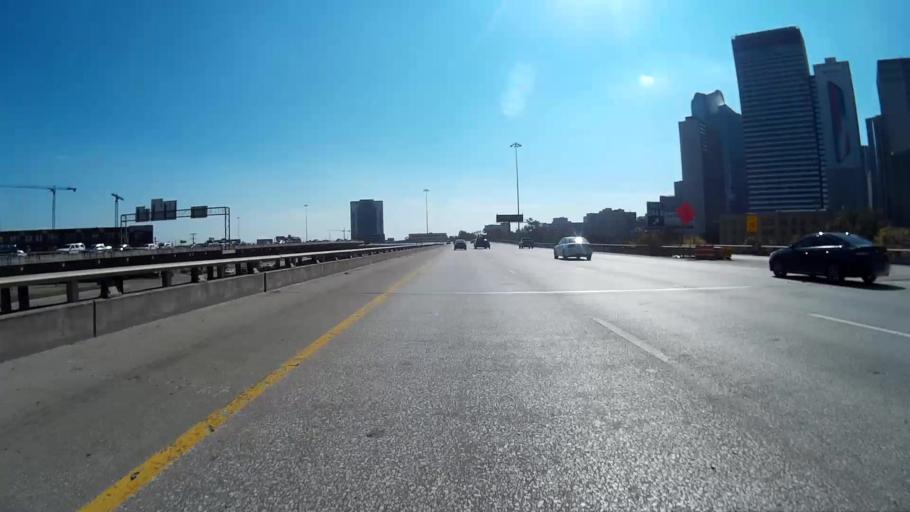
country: US
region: Texas
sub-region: Dallas County
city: Dallas
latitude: 32.7880
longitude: -96.7923
